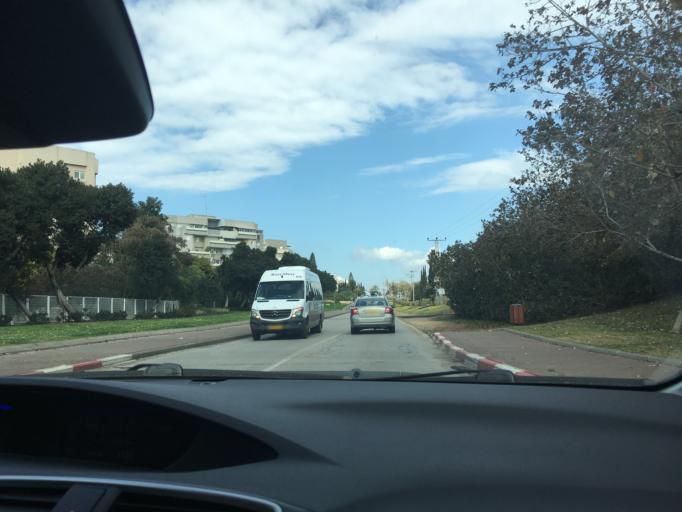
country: IL
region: Tel Aviv
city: Ramat HaSharon
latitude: 32.1633
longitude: 34.8531
